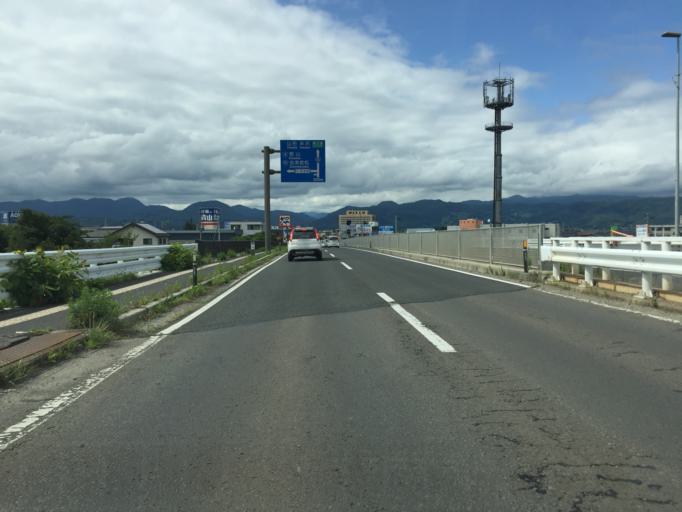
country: JP
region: Fukushima
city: Fukushima-shi
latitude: 37.7867
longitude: 140.4624
